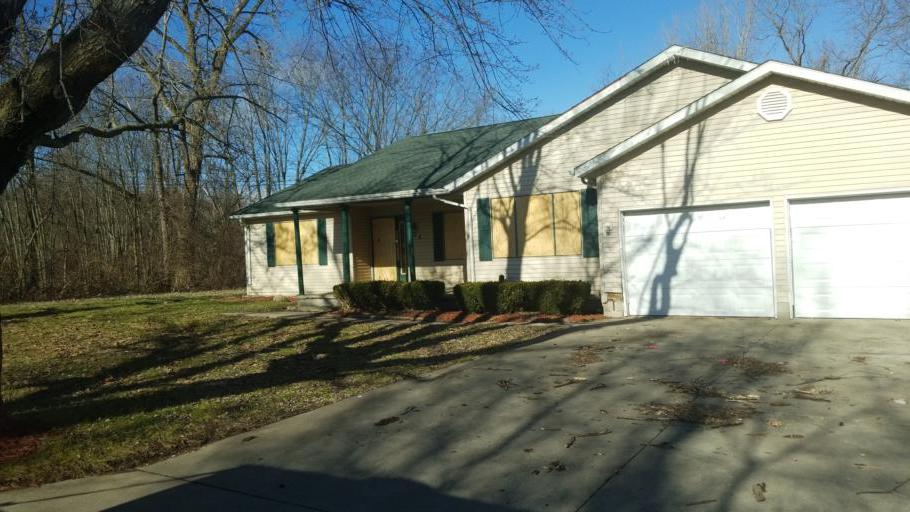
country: US
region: Ohio
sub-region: Richland County
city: Mansfield
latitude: 40.7790
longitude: -82.5262
